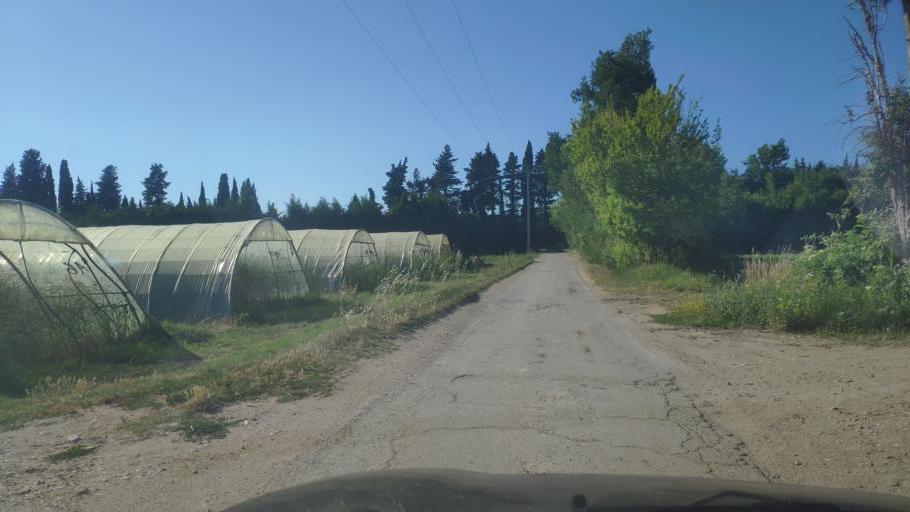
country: FR
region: Provence-Alpes-Cote d'Azur
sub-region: Departement du Vaucluse
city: Aubignan
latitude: 44.0805
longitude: 5.0208
